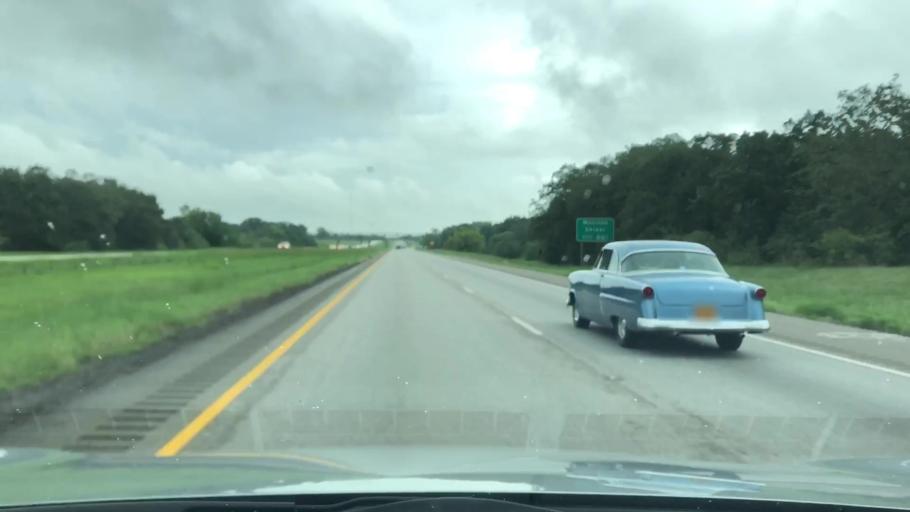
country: US
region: Texas
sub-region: Fayette County
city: Flatonia
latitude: 29.6966
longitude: -97.1179
